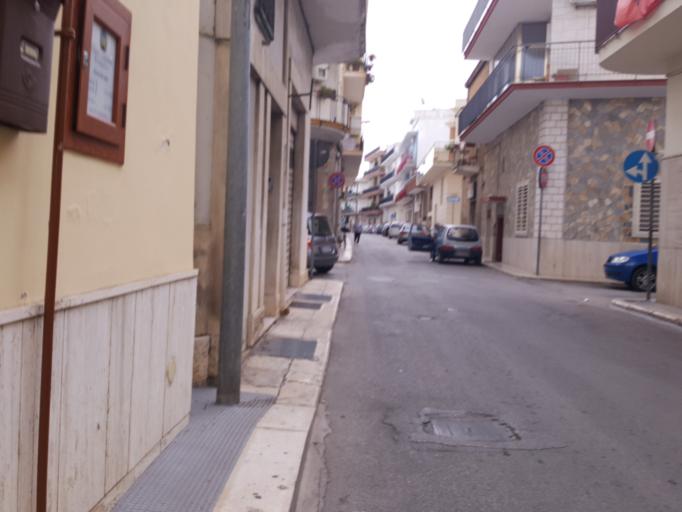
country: IT
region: Apulia
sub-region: Provincia di Bari
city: Triggiano
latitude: 41.0620
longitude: 16.9263
